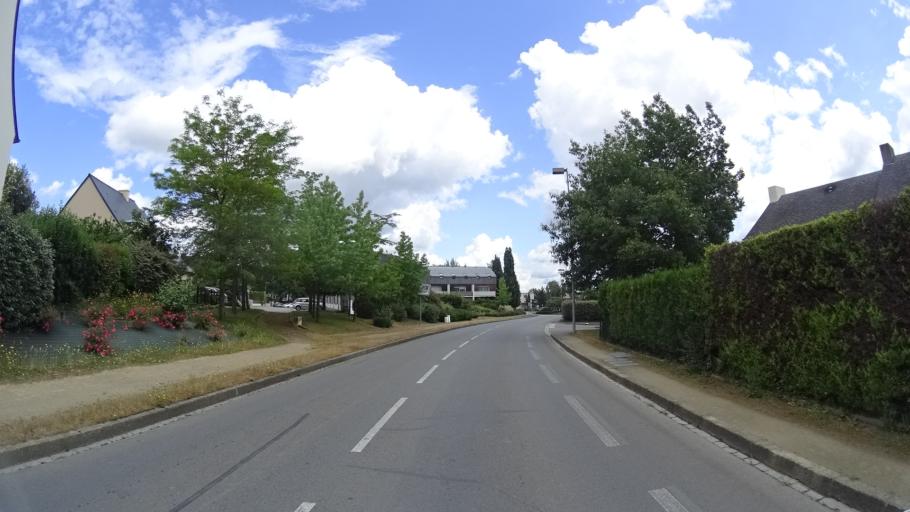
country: FR
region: Brittany
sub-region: Departement d'Ille-et-Vilaine
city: Chartres-de-Bretagne
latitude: 48.0401
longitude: -1.6973
